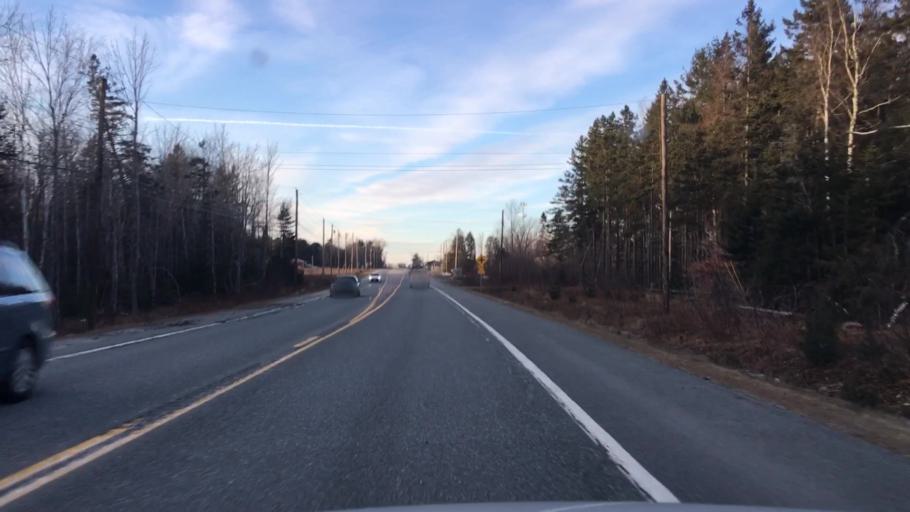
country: US
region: Maine
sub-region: Hancock County
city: Surry
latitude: 44.6130
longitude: -68.5225
